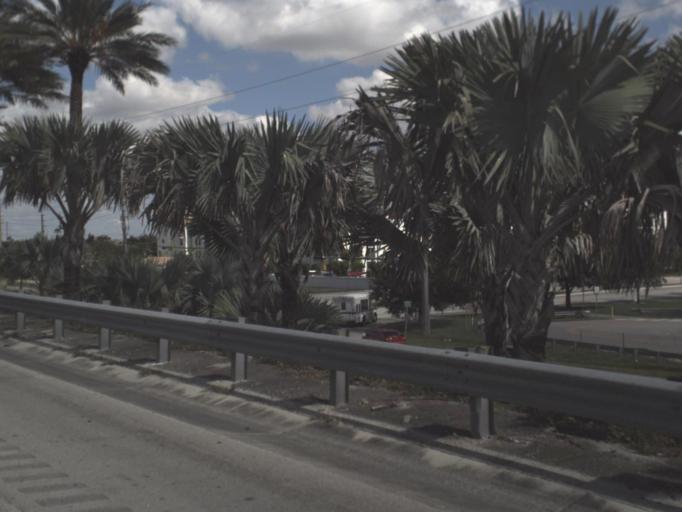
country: US
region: Florida
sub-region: Miami-Dade County
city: Doral
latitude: 25.8109
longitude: -80.3862
